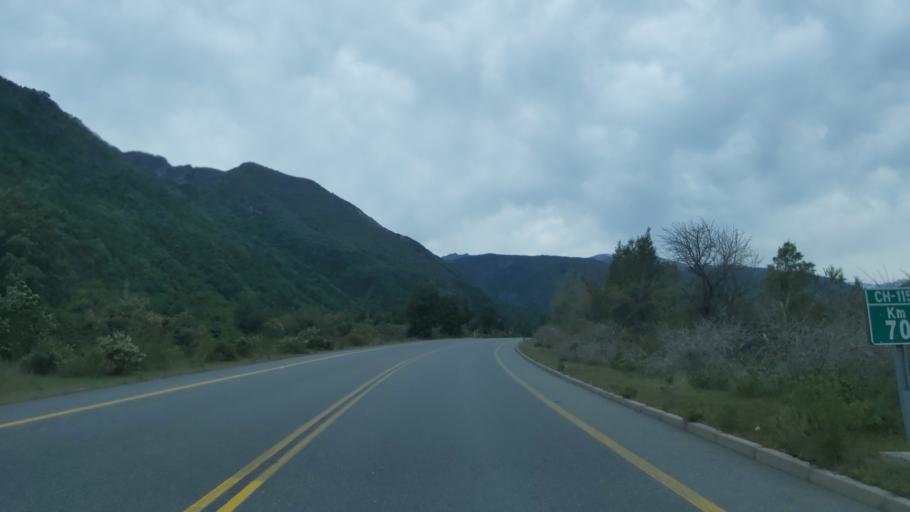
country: CL
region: Maule
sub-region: Provincia de Linares
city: Colbun
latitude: -35.7120
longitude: -71.0587
